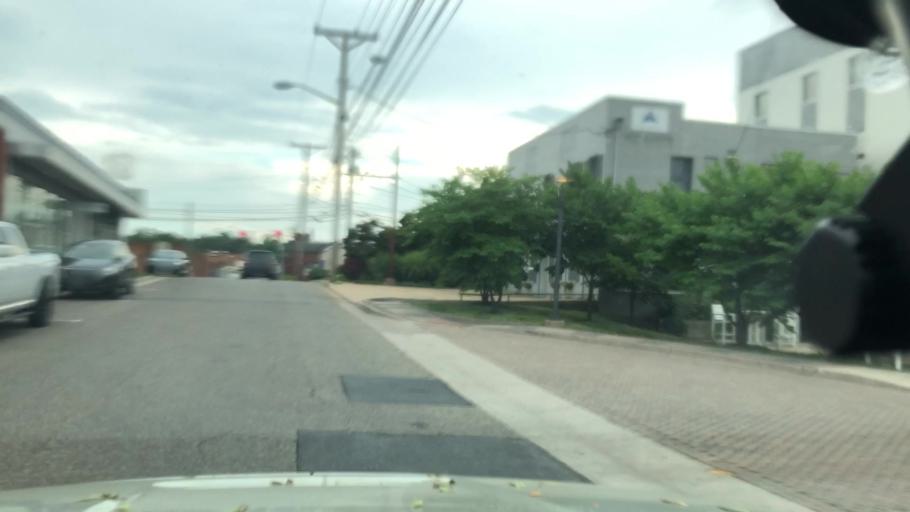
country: US
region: Virginia
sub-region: City of Harrisonburg
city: Harrisonburg
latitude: 38.4478
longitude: -78.8721
